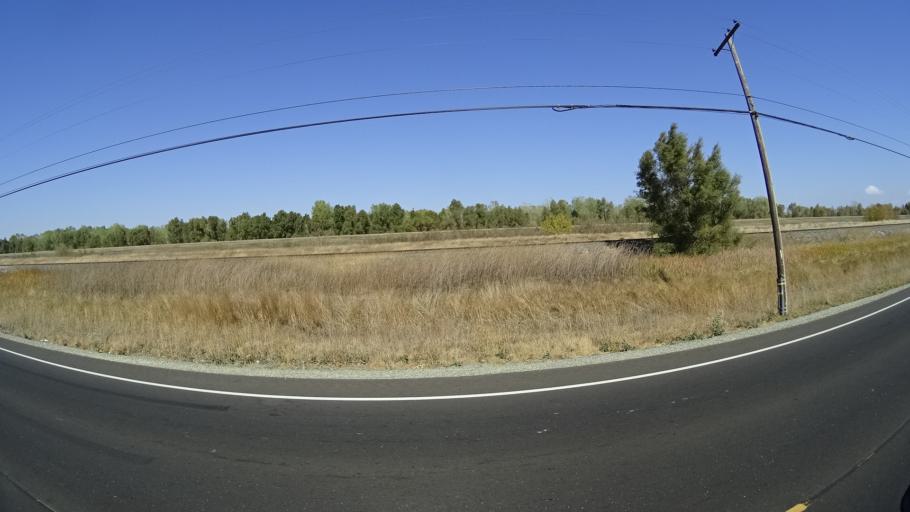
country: US
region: California
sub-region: Yolo County
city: Woodland
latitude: 38.6767
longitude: -121.6950
